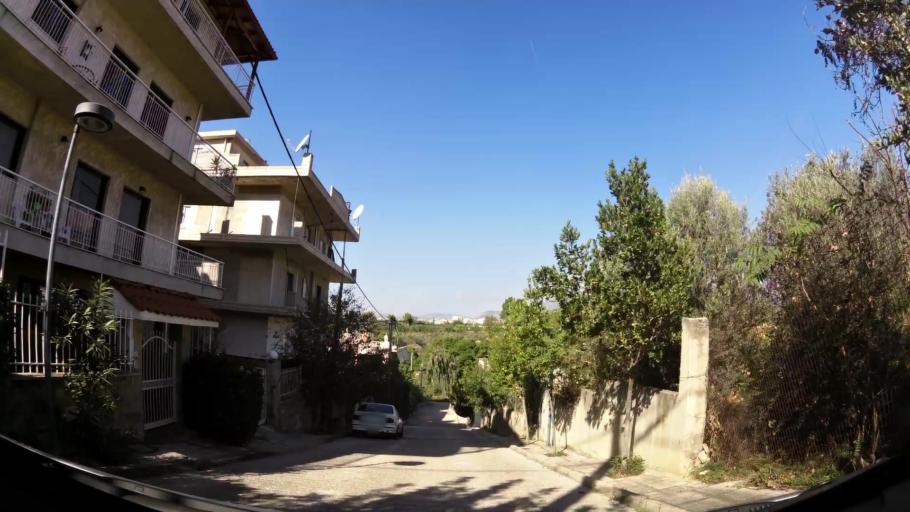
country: GR
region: Attica
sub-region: Nomarchia Athinas
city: Metamorfosi
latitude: 38.0684
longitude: 23.7545
